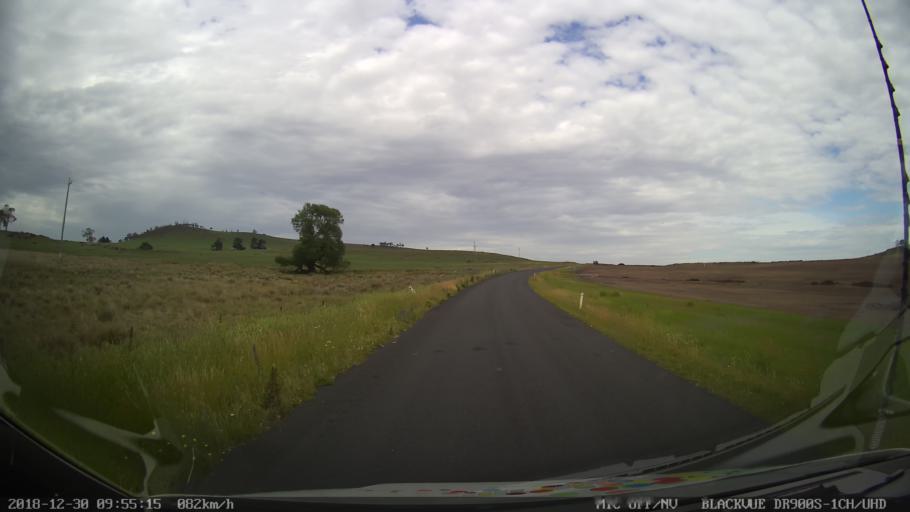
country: AU
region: New South Wales
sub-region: Cooma-Monaro
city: Cooma
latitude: -36.5203
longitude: 149.2673
